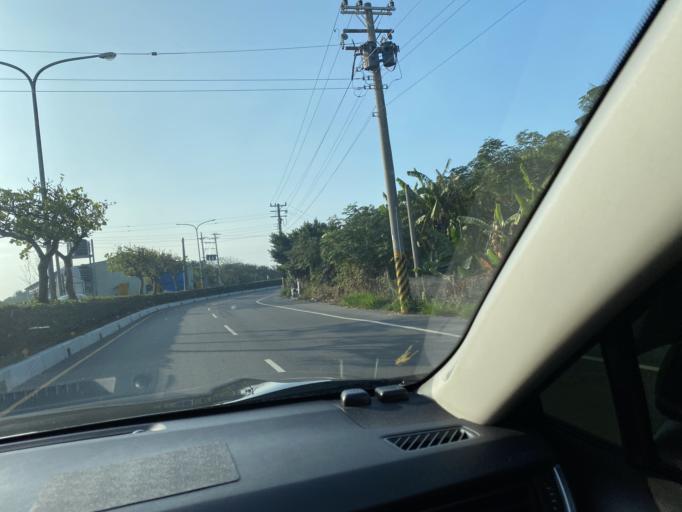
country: TW
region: Taiwan
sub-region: Changhua
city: Chang-hua
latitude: 23.9617
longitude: 120.3520
